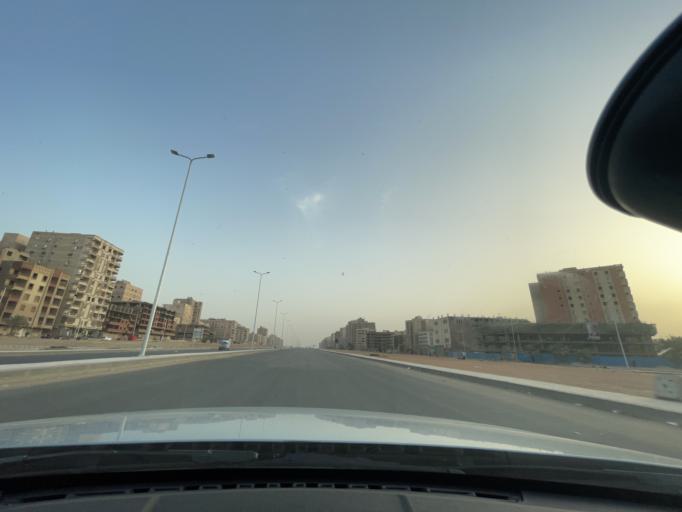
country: EG
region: Muhafazat al Qahirah
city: Cairo
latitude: 30.0573
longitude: 31.3748
